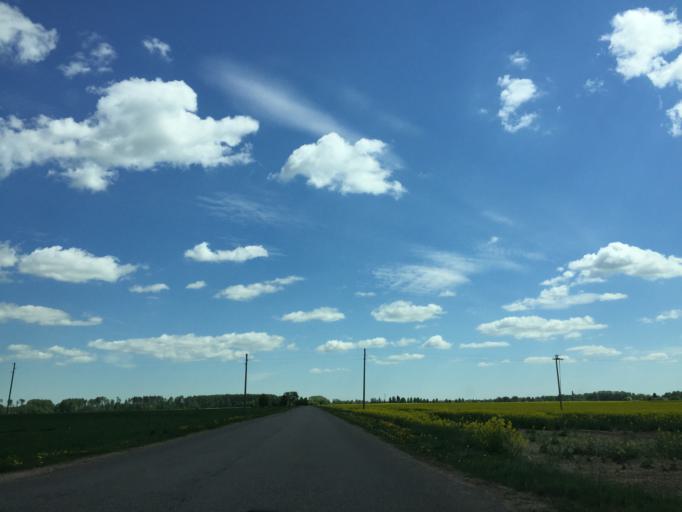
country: LV
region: Rundales
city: Pilsrundale
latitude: 56.4305
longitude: 24.0857
